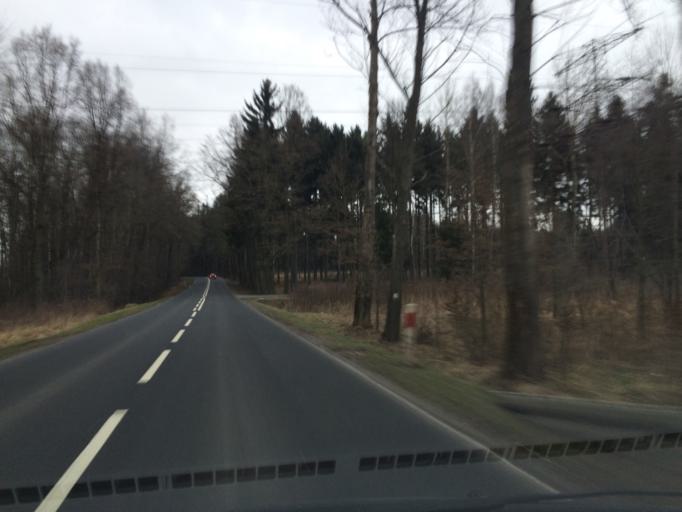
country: PL
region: Lower Silesian Voivodeship
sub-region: Powiat lubanski
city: Luban
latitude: 51.1454
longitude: 15.2731
